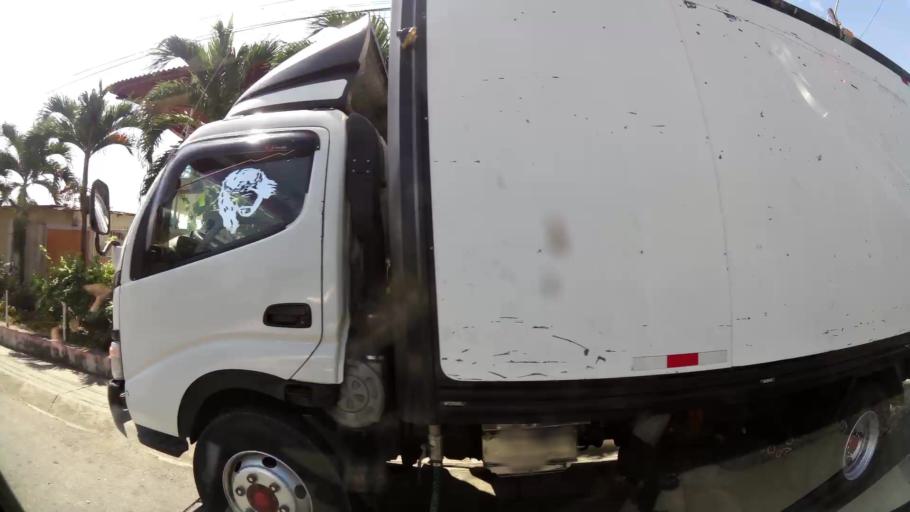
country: EC
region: Guayas
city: Guayaquil
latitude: -2.1294
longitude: -79.9212
